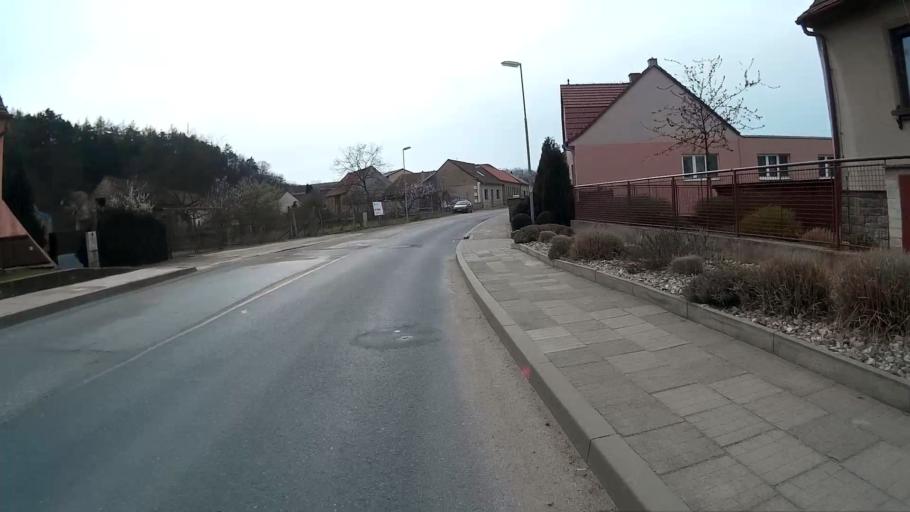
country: CZ
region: South Moravian
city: Dolni Kounice
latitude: 49.0702
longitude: 16.4461
